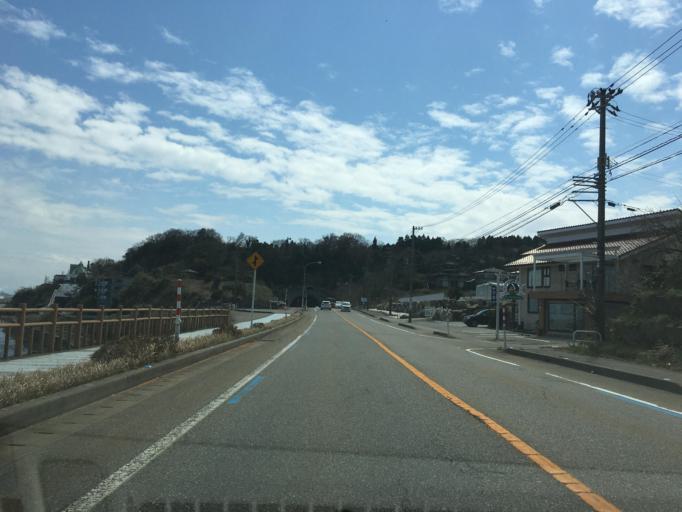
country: JP
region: Toyama
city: Nishishinminato
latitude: 36.8114
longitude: 137.0468
